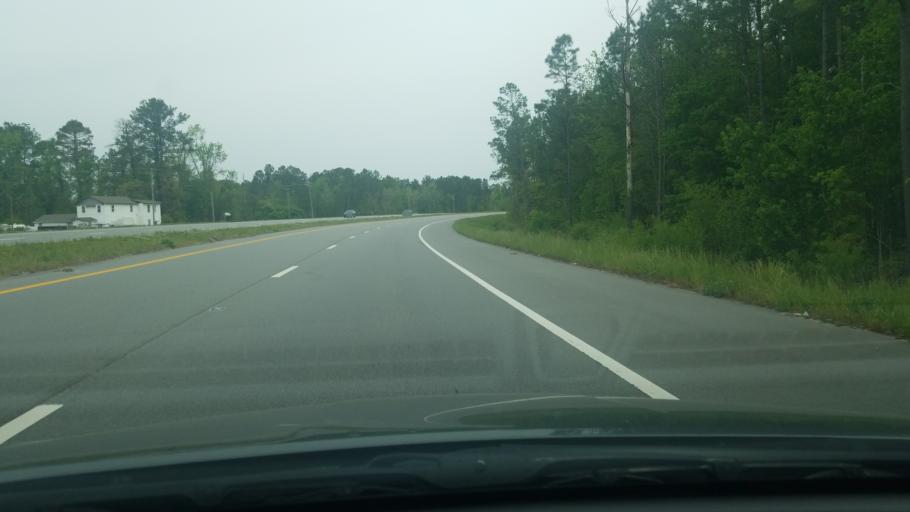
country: US
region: North Carolina
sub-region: Jones County
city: Maysville
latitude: 34.9491
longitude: -77.2418
